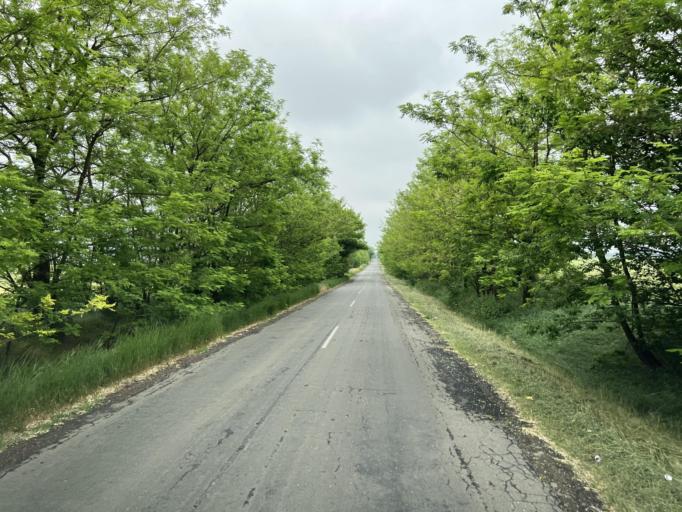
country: HU
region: Pest
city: Tura
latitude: 47.6187
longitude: 19.6354
